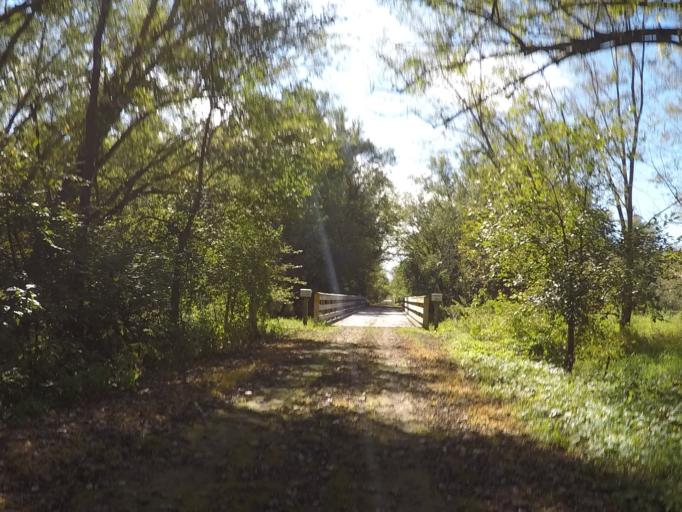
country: US
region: Wisconsin
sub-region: Richland County
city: Richland Center
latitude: 43.2849
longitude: -90.3205
